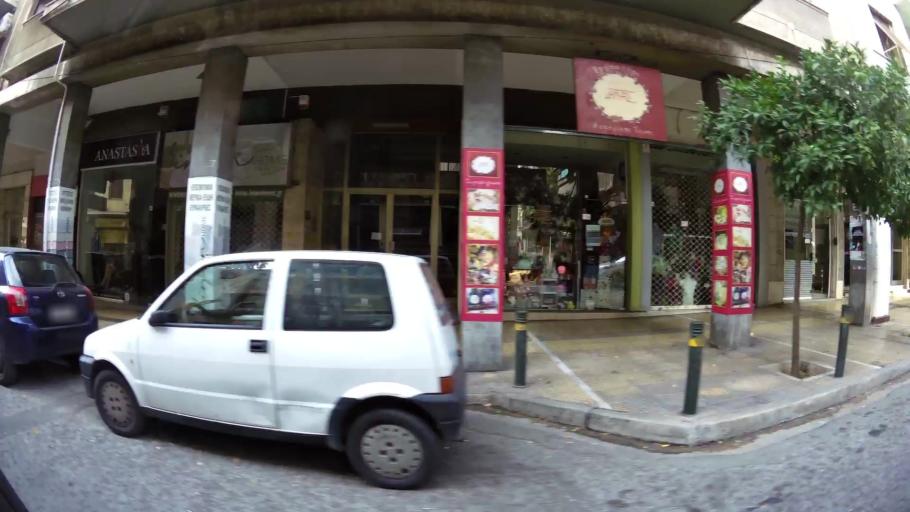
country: GR
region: Attica
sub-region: Nomarchia Athinas
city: Kipseli
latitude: 38.0012
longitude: 23.7407
